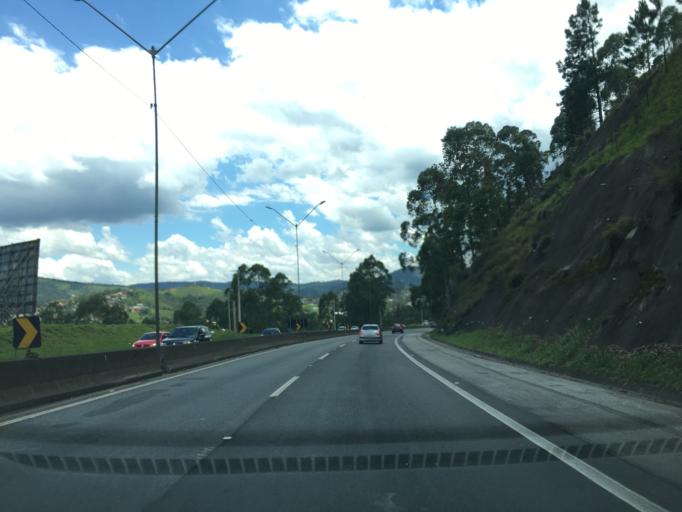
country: BR
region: Sao Paulo
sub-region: Mairipora
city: Mairipora
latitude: -23.3009
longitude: -46.5720
